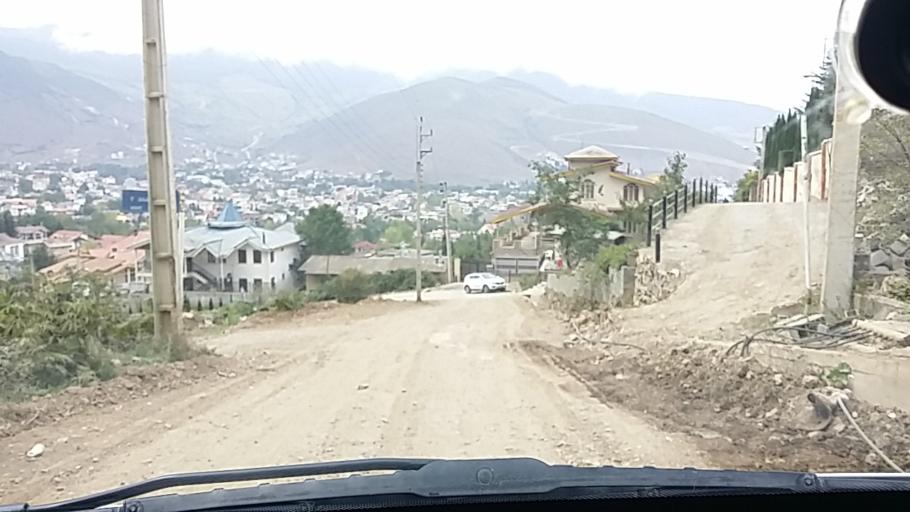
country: IR
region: Mazandaran
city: `Abbasabad
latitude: 36.4924
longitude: 51.1664
